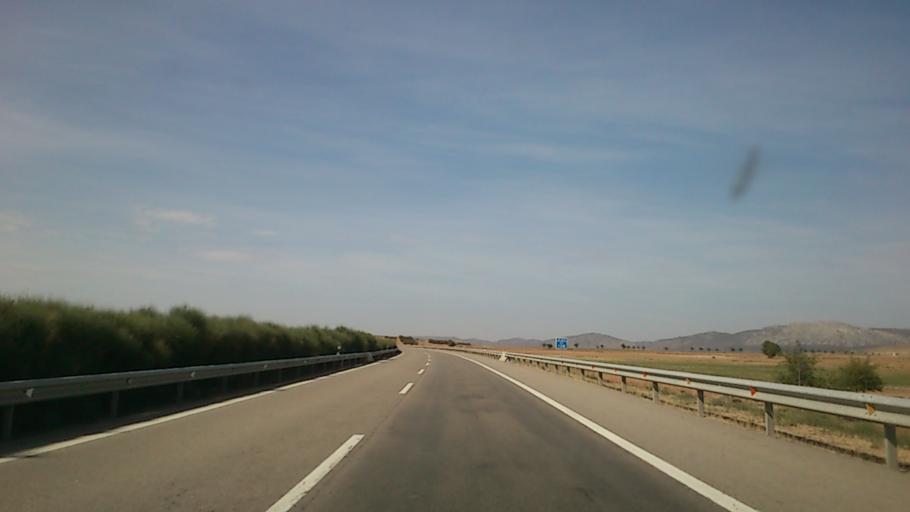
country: ES
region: Aragon
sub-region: Provincia de Teruel
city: Villarquemado
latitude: 40.5133
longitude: -1.2536
